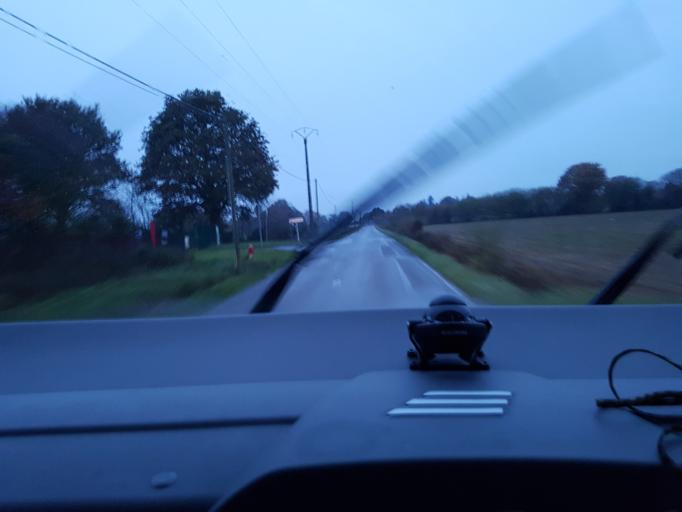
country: FR
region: Brittany
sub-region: Departement d'Ille-et-Vilaine
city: Montreuil-sous-Perouse
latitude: 48.1934
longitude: -1.2768
